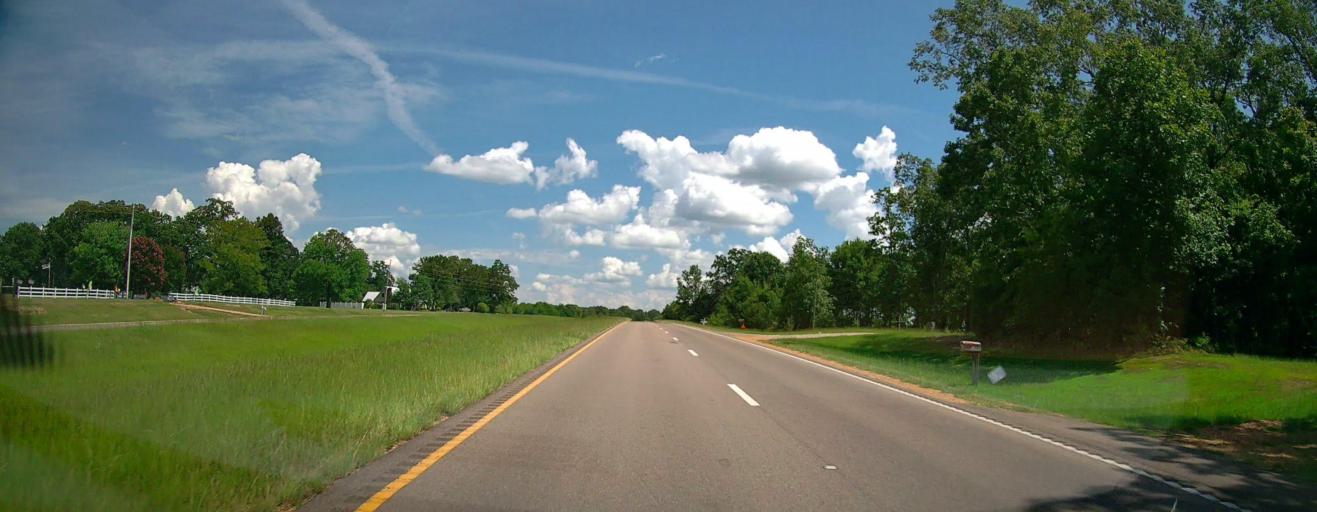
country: US
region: Mississippi
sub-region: Monroe County
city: Amory
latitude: 33.9592
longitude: -88.6107
